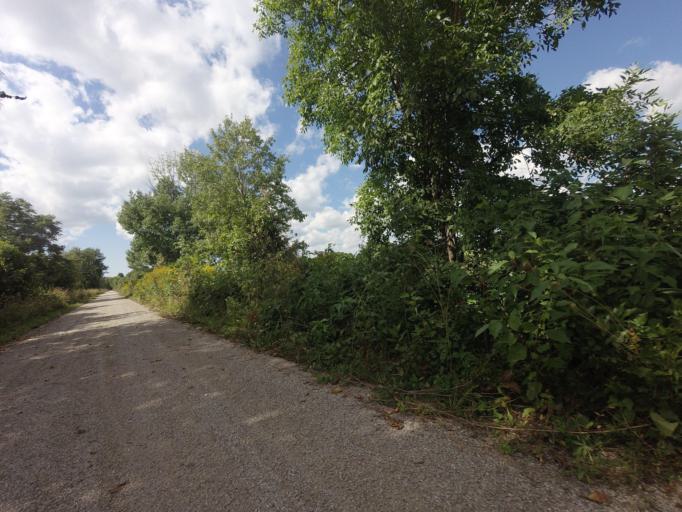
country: CA
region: Ontario
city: Huron East
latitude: 43.7211
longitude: -81.3988
